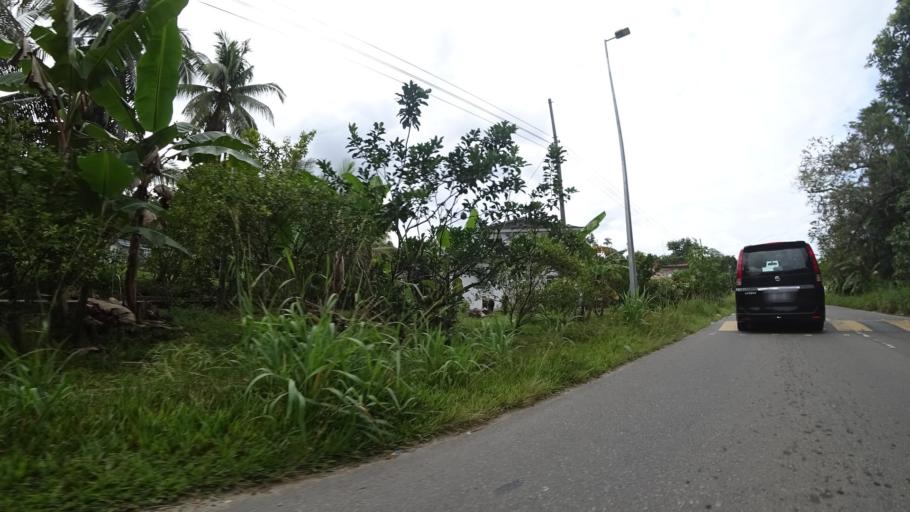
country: BN
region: Brunei and Muara
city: Bandar Seri Begawan
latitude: 4.8661
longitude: 114.9433
